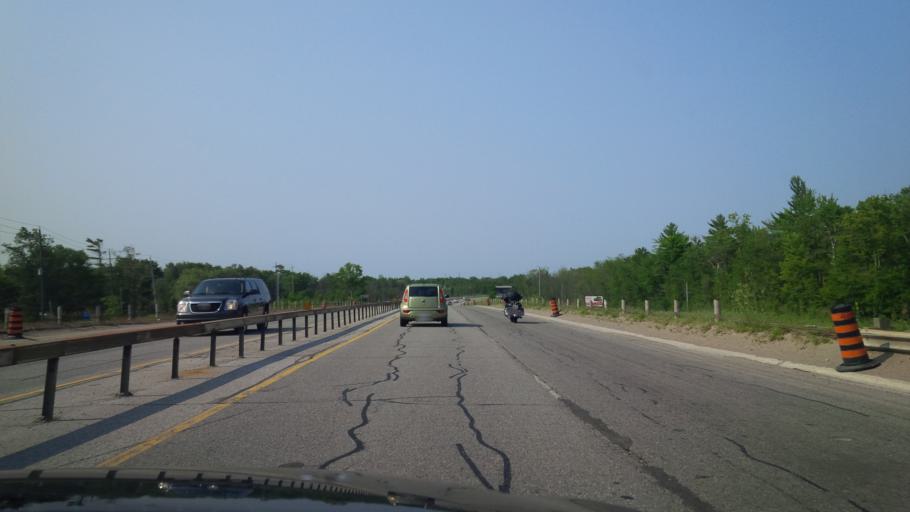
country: CA
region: Ontario
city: Orillia
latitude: 44.7480
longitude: -79.3426
